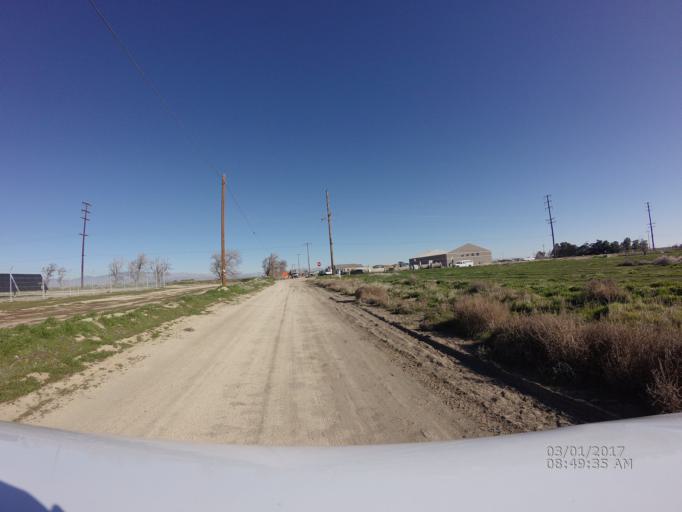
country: US
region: California
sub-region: Los Angeles County
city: Quartz Hill
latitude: 34.7179
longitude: -118.2721
